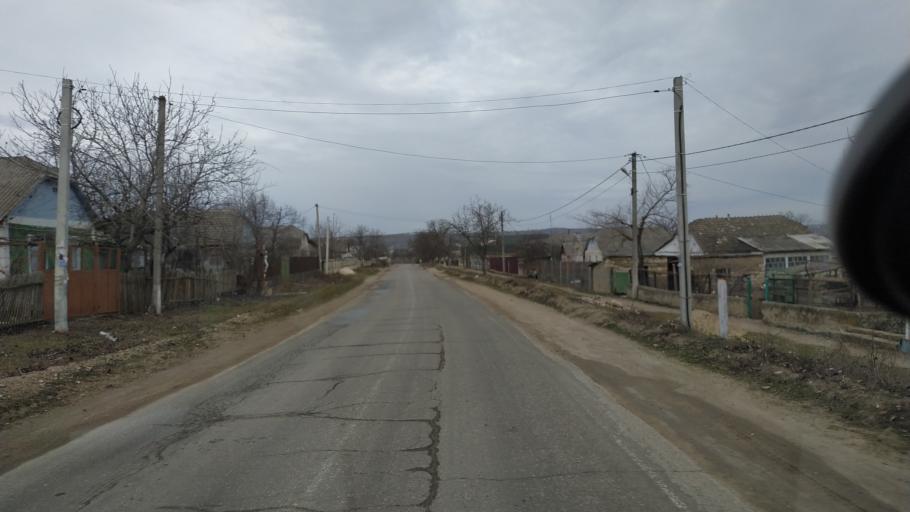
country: MD
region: Telenesti
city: Dubasari
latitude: 47.2458
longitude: 29.1407
